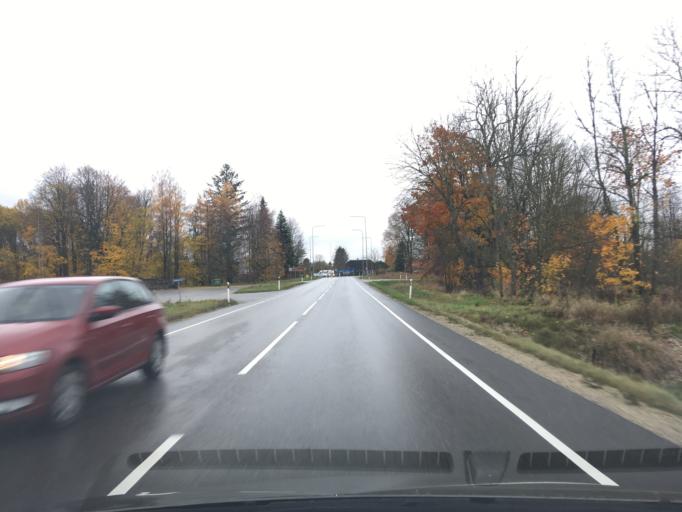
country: EE
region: Jogevamaa
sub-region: Tabivere vald
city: Tabivere
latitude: 58.4318
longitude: 26.4864
